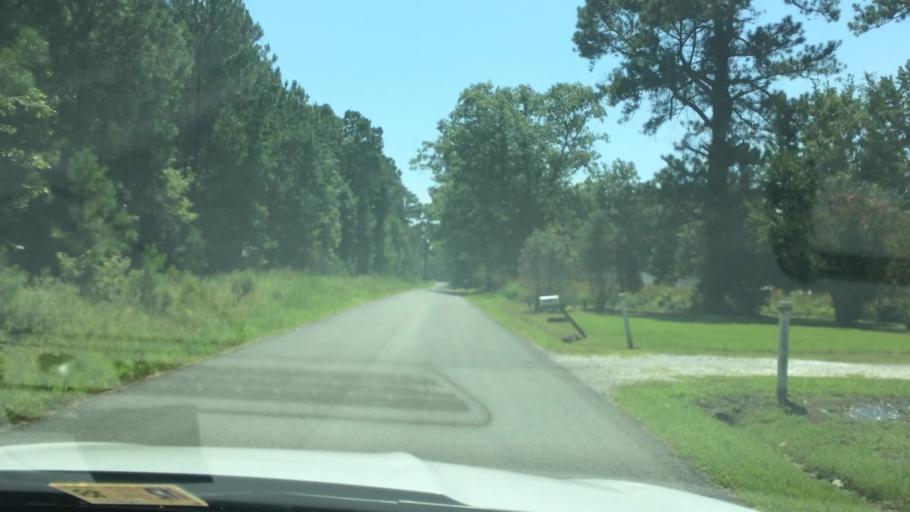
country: US
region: Virginia
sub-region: Charles City County
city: Charles City
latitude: 37.2968
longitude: -76.9656
